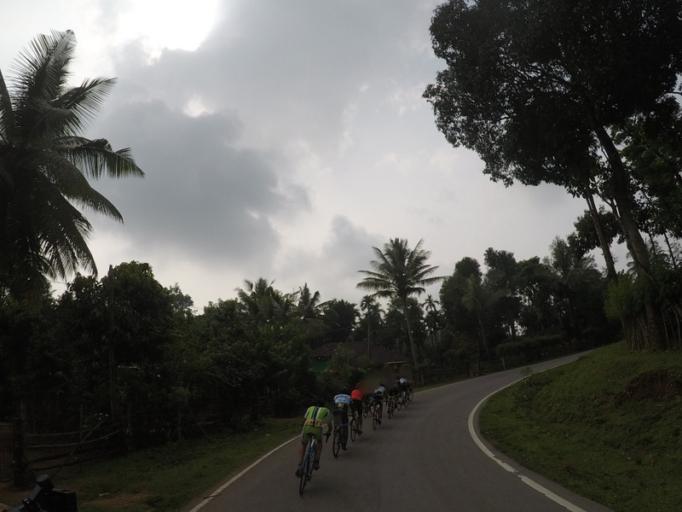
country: IN
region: Karnataka
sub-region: Chikmagalur
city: Mudigere
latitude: 13.2754
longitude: 75.4724
